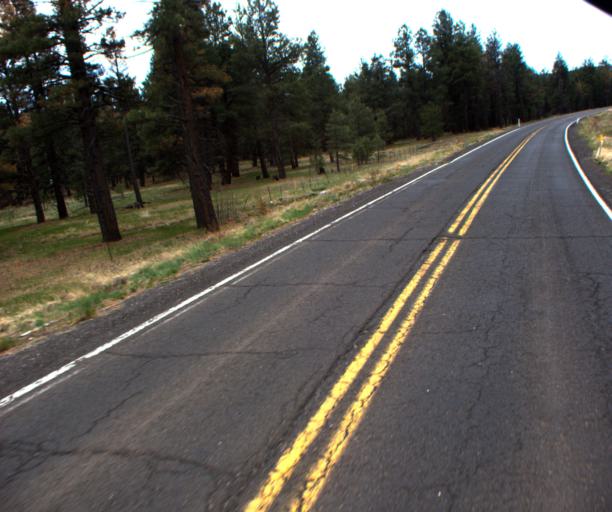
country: US
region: Arizona
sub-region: Coconino County
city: Kachina Village
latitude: 35.1251
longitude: -111.6936
